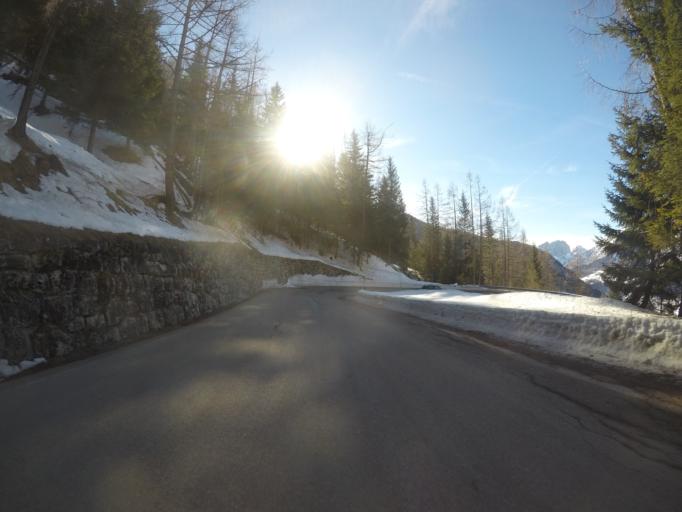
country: IT
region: Veneto
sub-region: Provincia di Belluno
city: Livinallongo del Col di Lana
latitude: 46.4904
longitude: 11.9906
